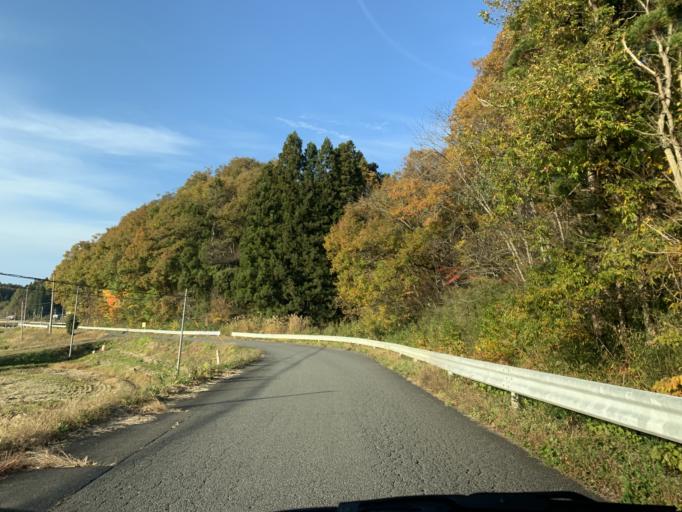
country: JP
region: Iwate
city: Ichinoseki
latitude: 38.9430
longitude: 141.0637
